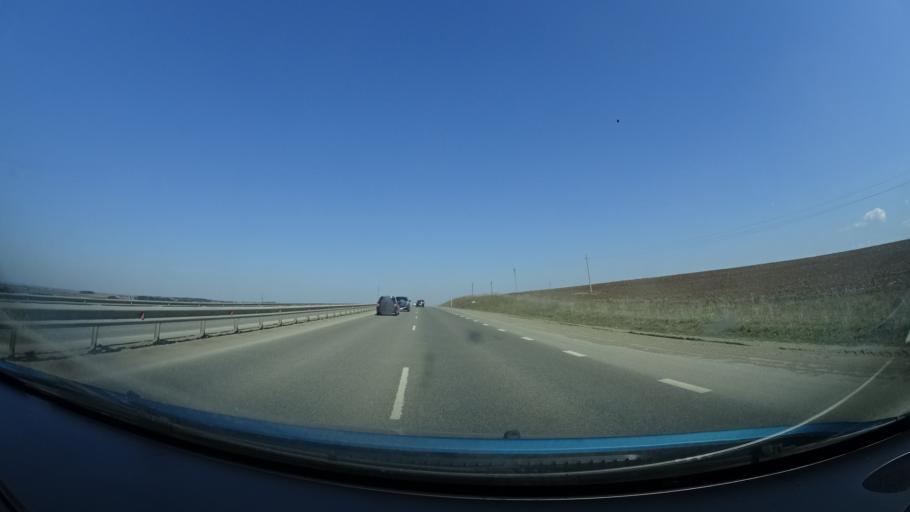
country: RU
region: Perm
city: Kultayevo
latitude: 57.8674
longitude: 55.8863
